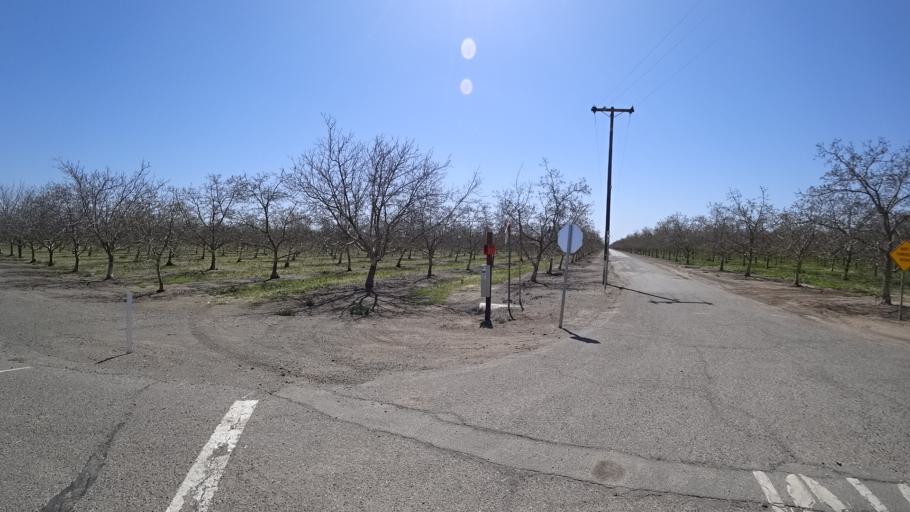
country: US
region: California
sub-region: Butte County
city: Durham
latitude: 39.4641
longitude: -121.9395
